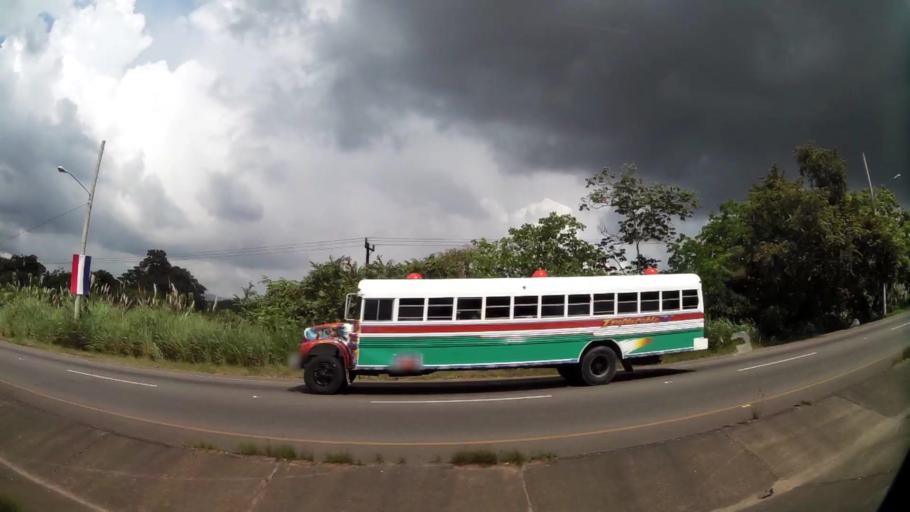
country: PA
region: Panama
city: Cabra Numero Uno
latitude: 9.1013
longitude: -79.3424
